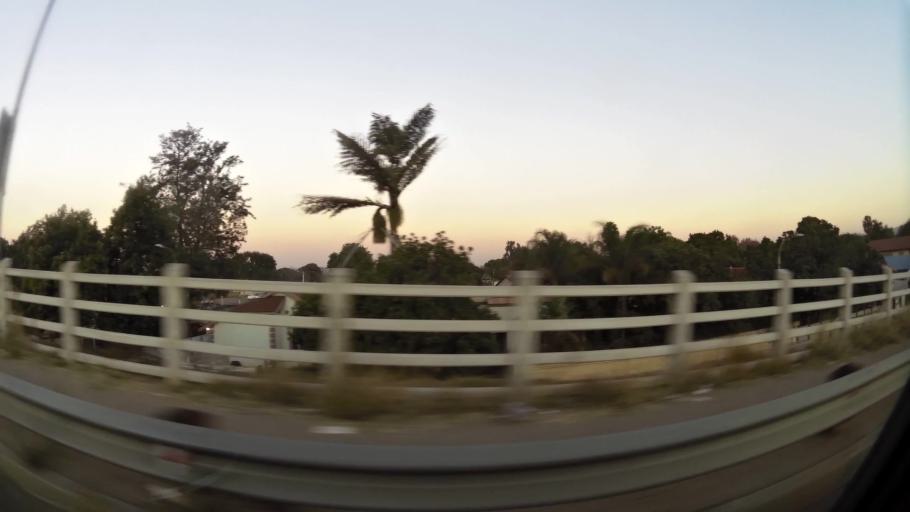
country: ZA
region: North-West
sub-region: Bojanala Platinum District Municipality
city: Rustenburg
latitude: -25.6564
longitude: 27.2435
